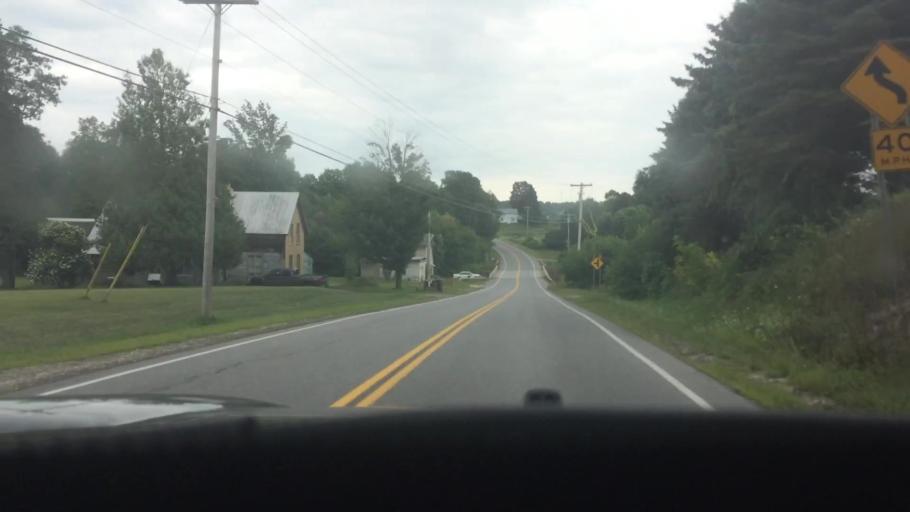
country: US
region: New York
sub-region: St. Lawrence County
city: Canton
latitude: 44.5583
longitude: -75.1155
